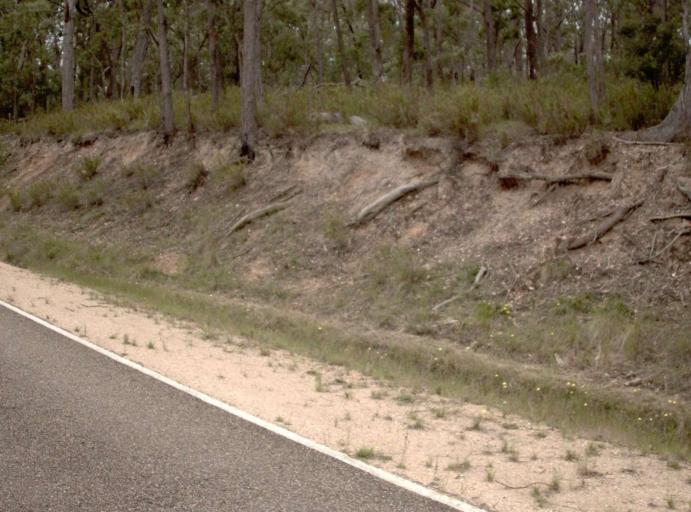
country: AU
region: Victoria
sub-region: East Gippsland
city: Bairnsdale
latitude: -37.7520
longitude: 147.3237
